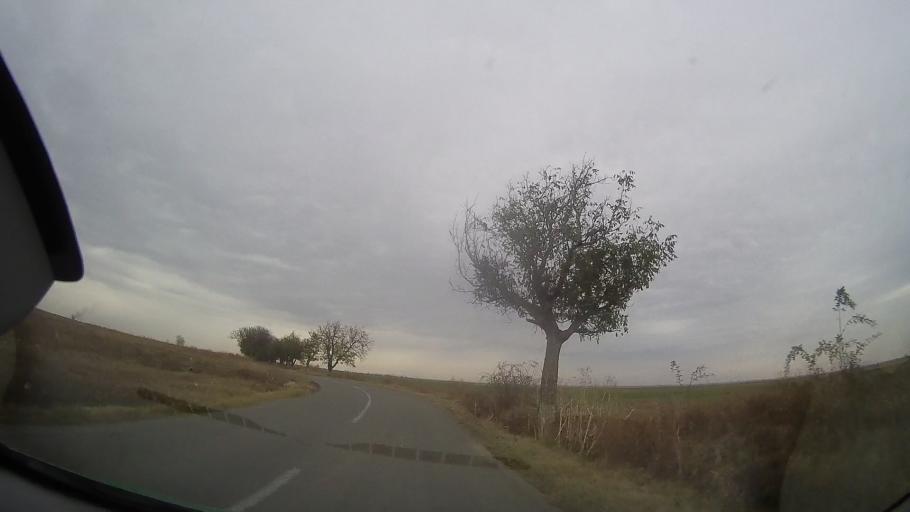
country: RO
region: Prahova
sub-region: Comuna Vadu Sapat
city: Vadu Sapat
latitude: 45.0198
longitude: 26.3949
